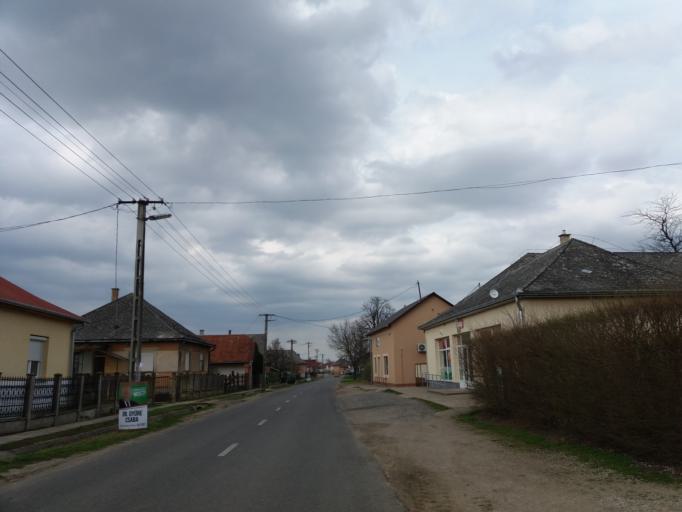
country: HU
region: Szabolcs-Szatmar-Bereg
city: Nyirtass
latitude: 48.1142
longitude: 22.0217
